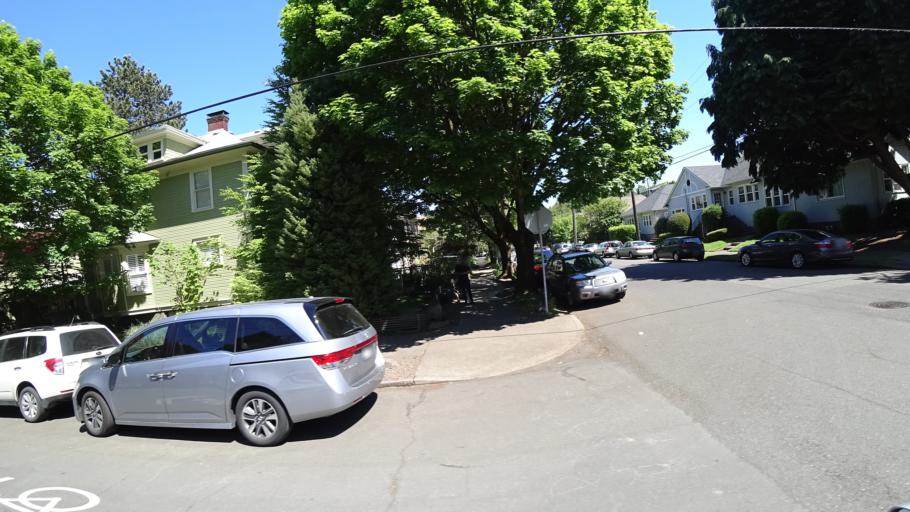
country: US
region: Oregon
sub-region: Multnomah County
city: Portland
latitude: 45.5130
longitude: -122.6361
